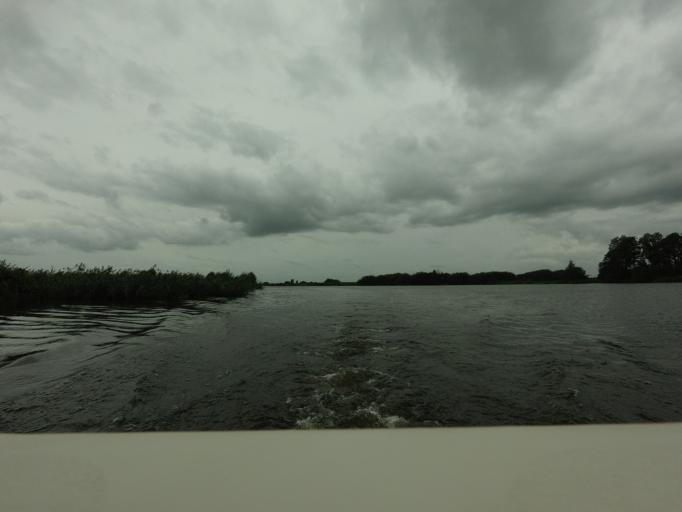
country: NL
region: Friesland
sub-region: Gemeente Boarnsterhim
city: Aldeboarn
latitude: 53.0949
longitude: 5.9268
